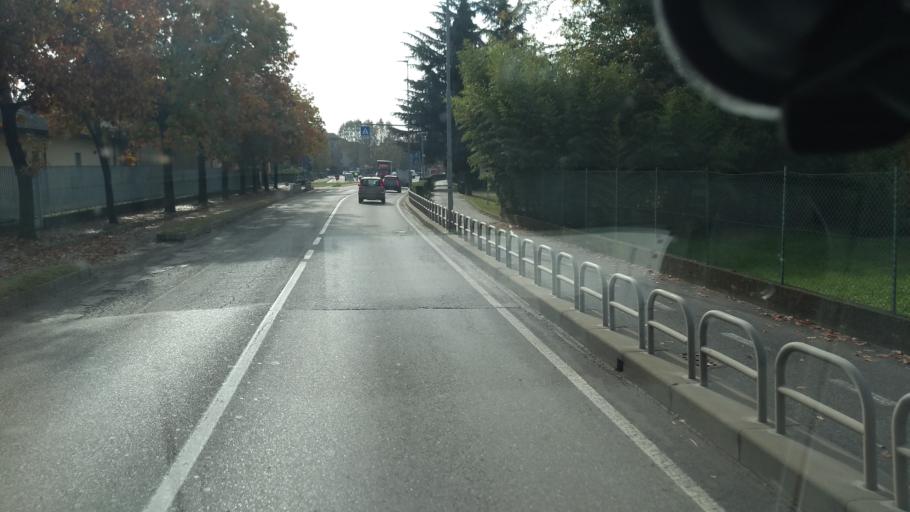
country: IT
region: Lombardy
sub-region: Provincia di Bergamo
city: Cologno al Serio
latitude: 45.5834
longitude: 9.7051
